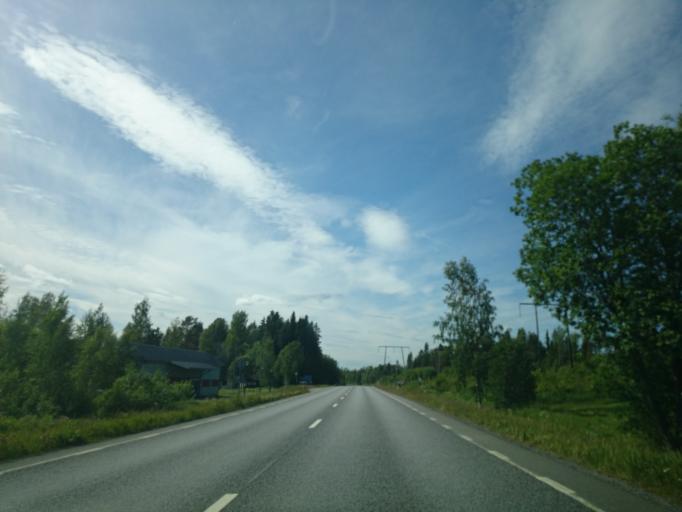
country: SE
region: Jaemtland
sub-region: Krokoms Kommun
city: Valla
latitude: 63.3345
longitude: 14.0203
